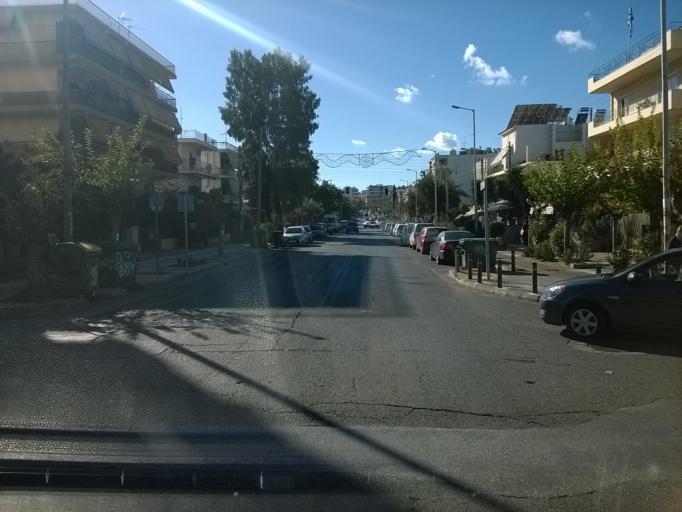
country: GR
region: Attica
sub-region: Nomarchia Athinas
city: Argyroupoli
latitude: 37.9034
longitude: 23.7503
